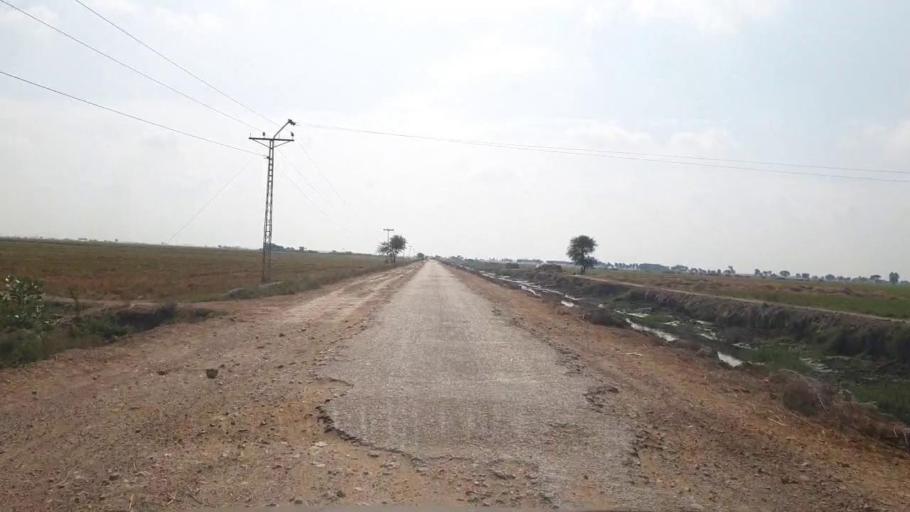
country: PK
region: Sindh
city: Kario
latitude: 24.6333
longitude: 68.5495
